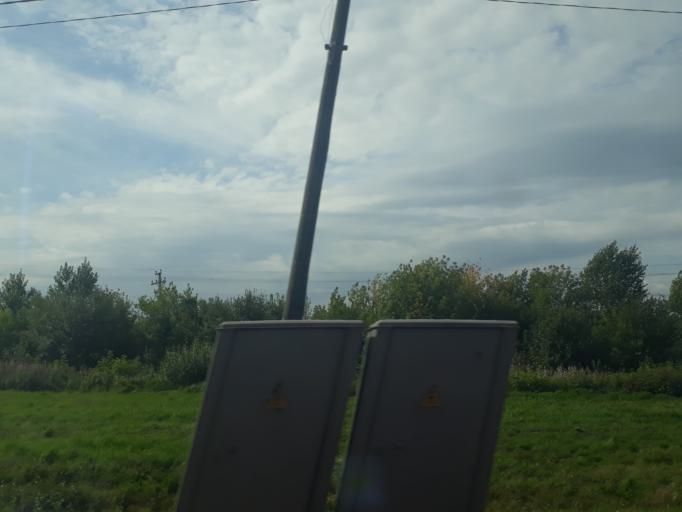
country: EE
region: Jogevamaa
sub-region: Jogeva linn
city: Jogeva
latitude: 58.8236
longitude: 26.3486
